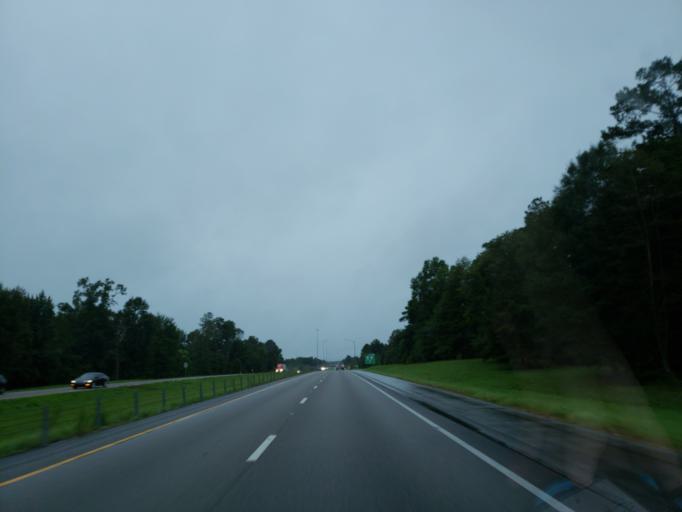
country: US
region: Mississippi
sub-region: Jones County
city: Ellisville
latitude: 31.6188
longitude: -89.2017
